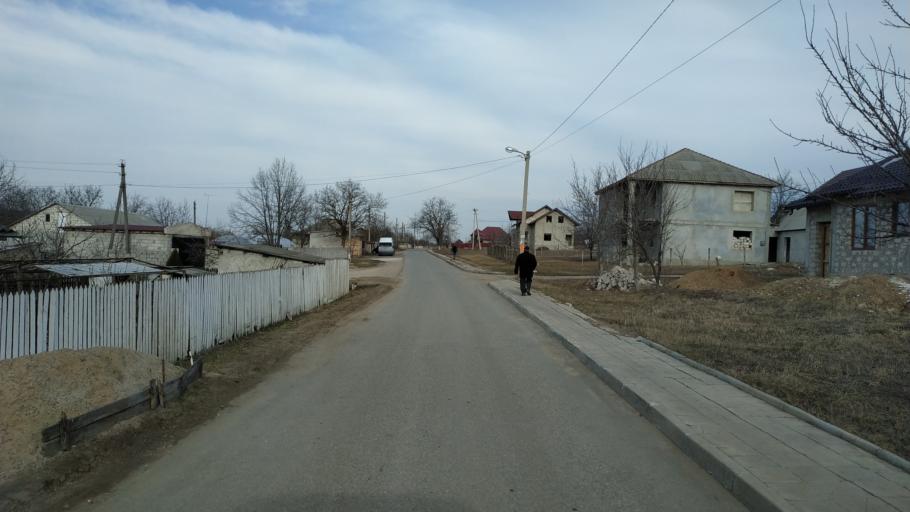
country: MD
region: Chisinau
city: Vatra
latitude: 46.9869
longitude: 28.6677
